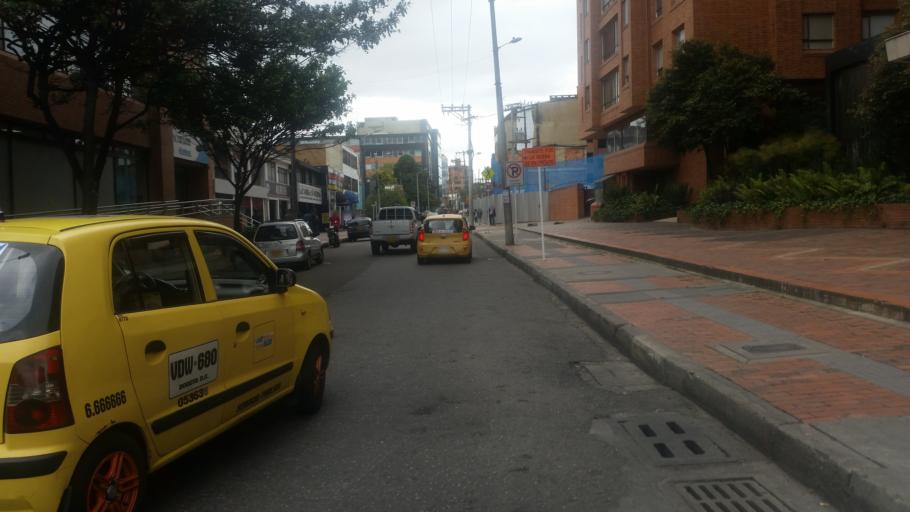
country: CO
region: Bogota D.C.
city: Barrio San Luis
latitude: 4.6645
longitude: -74.0573
